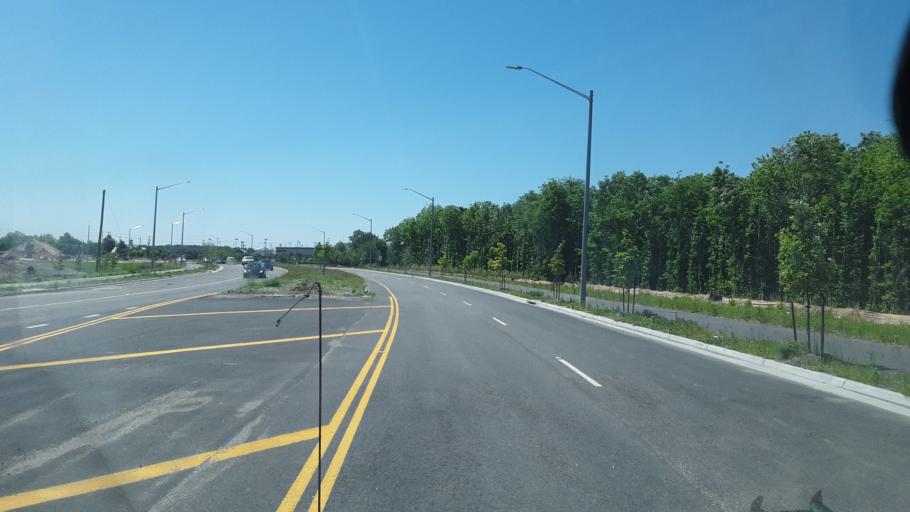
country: US
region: Virginia
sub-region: City of Virginia Beach
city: Virginia Beach
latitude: 36.7554
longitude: -76.0118
